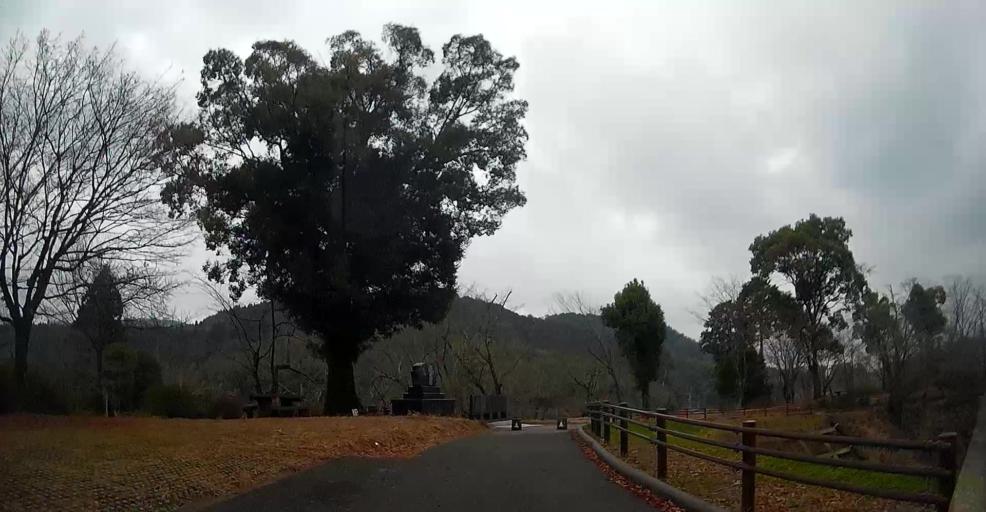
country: JP
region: Kumamoto
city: Matsubase
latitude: 32.6442
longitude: 130.7377
